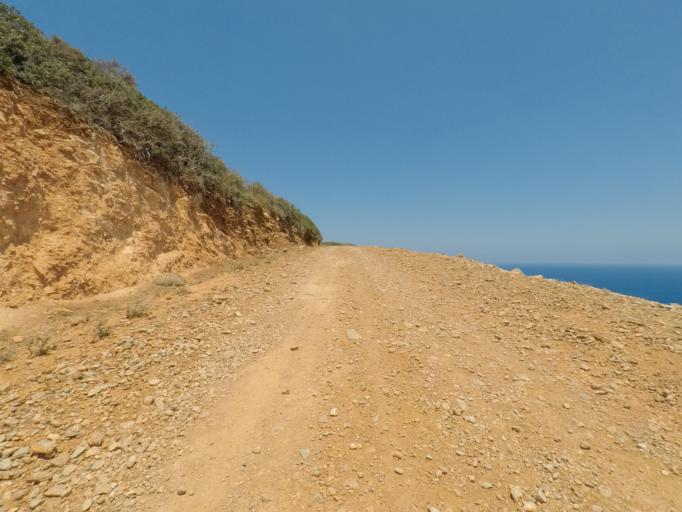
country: GR
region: Crete
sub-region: Nomos Lasithiou
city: Elounda
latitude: 35.3191
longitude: 25.7559
